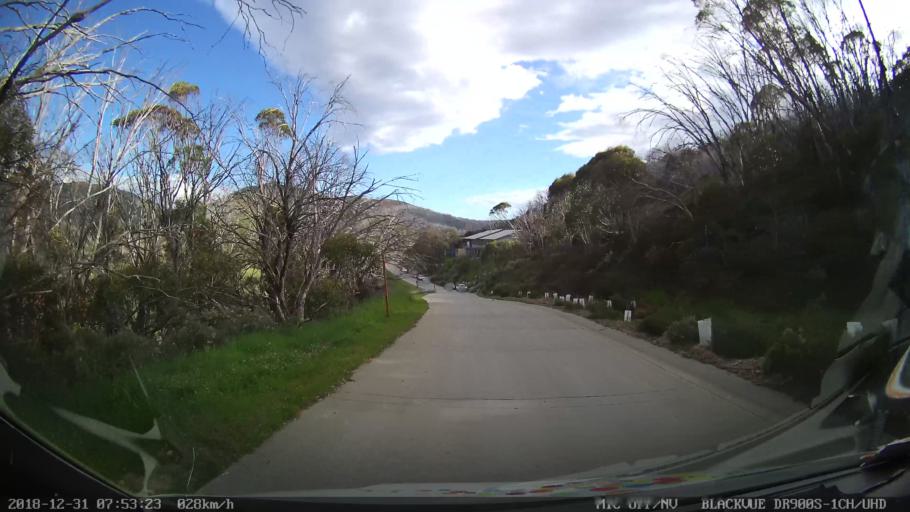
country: AU
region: New South Wales
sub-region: Snowy River
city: Jindabyne
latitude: -36.3809
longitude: 148.3734
